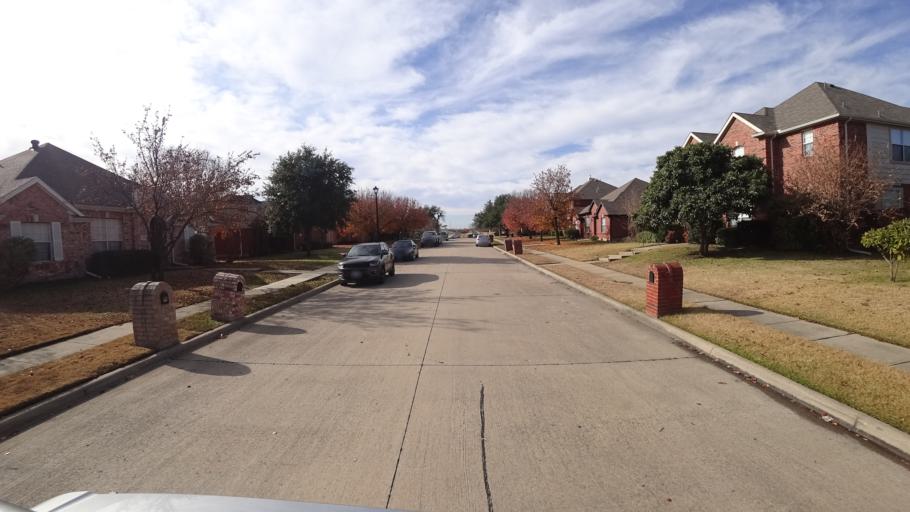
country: US
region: Texas
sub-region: Denton County
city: Lewisville
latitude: 33.0161
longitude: -96.9401
